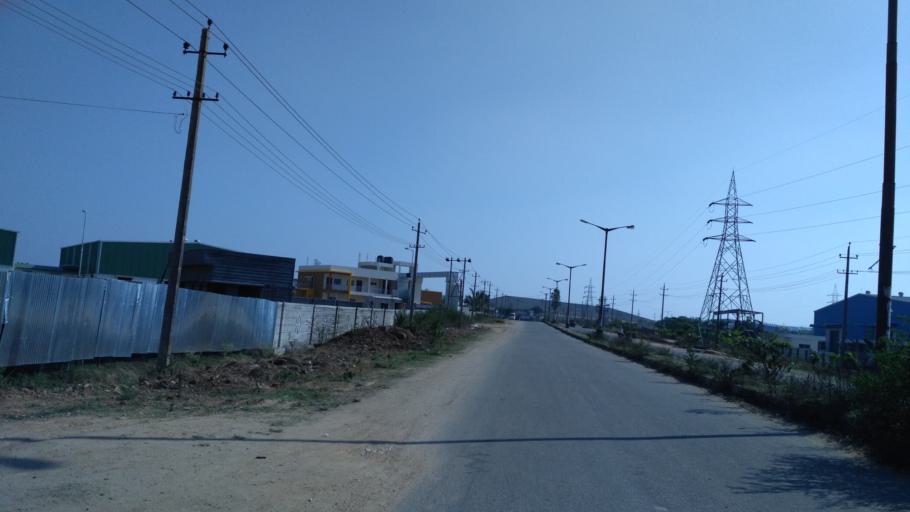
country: IN
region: Karnataka
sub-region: Hassan
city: Hassan
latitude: 12.9794
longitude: 76.1206
